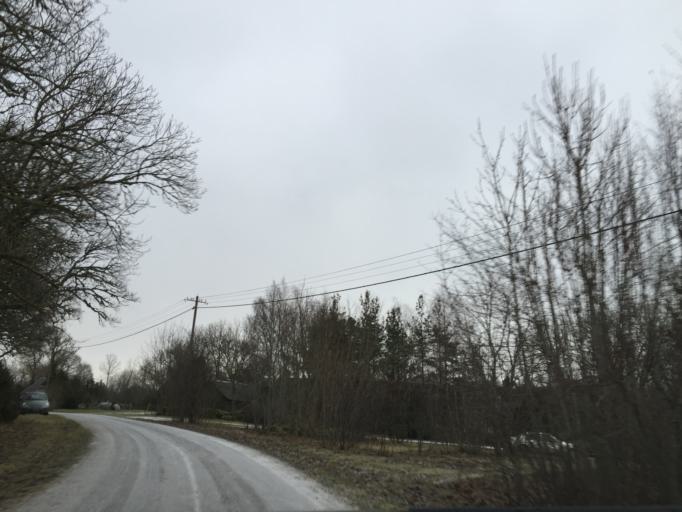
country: EE
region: Saare
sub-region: Orissaare vald
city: Orissaare
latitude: 58.5959
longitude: 23.0790
